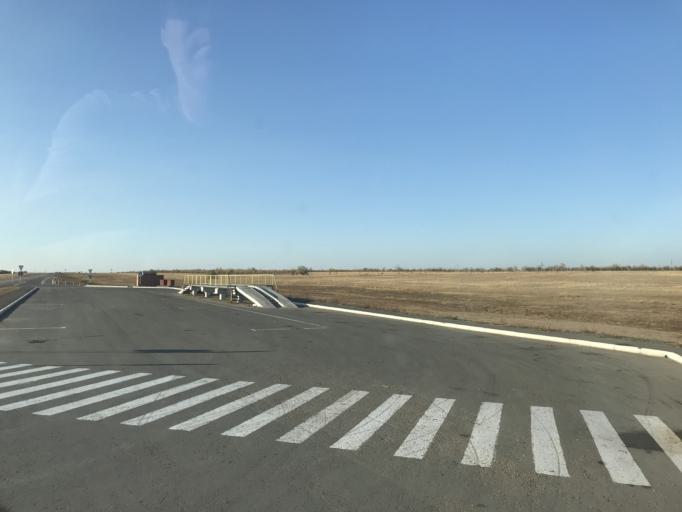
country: KZ
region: Pavlodar
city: Koktobe
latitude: 51.8825
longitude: 77.4193
